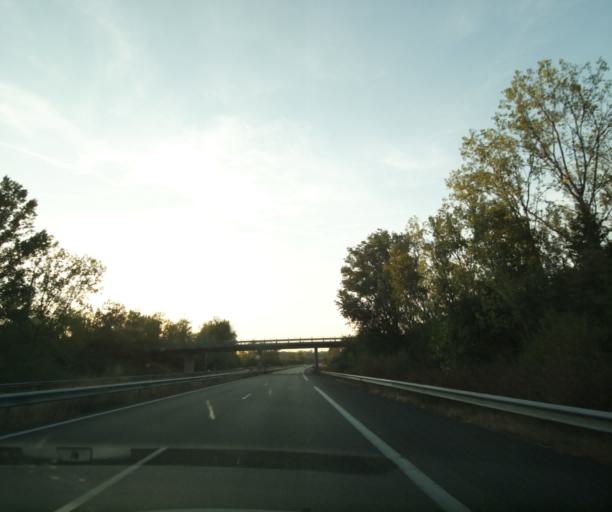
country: FR
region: Aquitaine
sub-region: Departement du Lot-et-Garonne
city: Fourques-sur-Garonne
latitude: 44.4302
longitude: 0.1363
